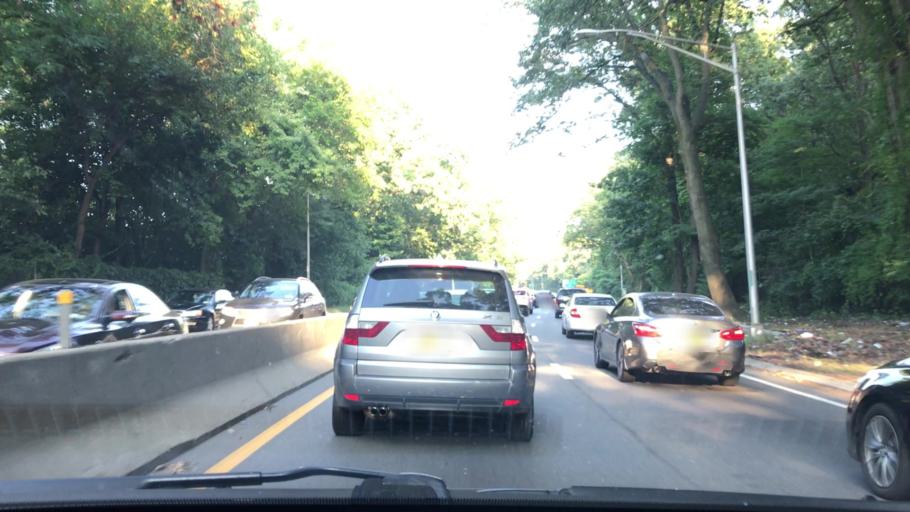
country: US
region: New York
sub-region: Queens County
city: Borough of Queens
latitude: 40.7078
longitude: -73.8489
